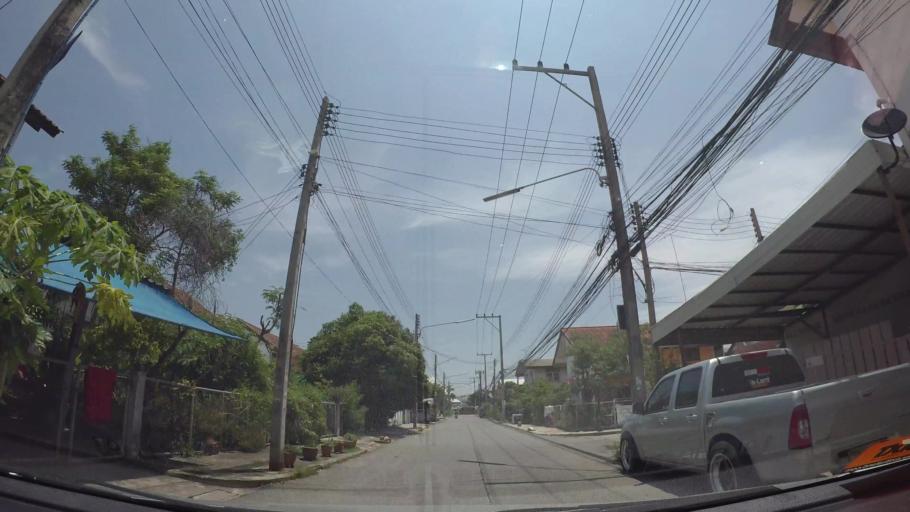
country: TH
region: Chon Buri
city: Chon Buri
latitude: 13.3273
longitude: 100.9416
